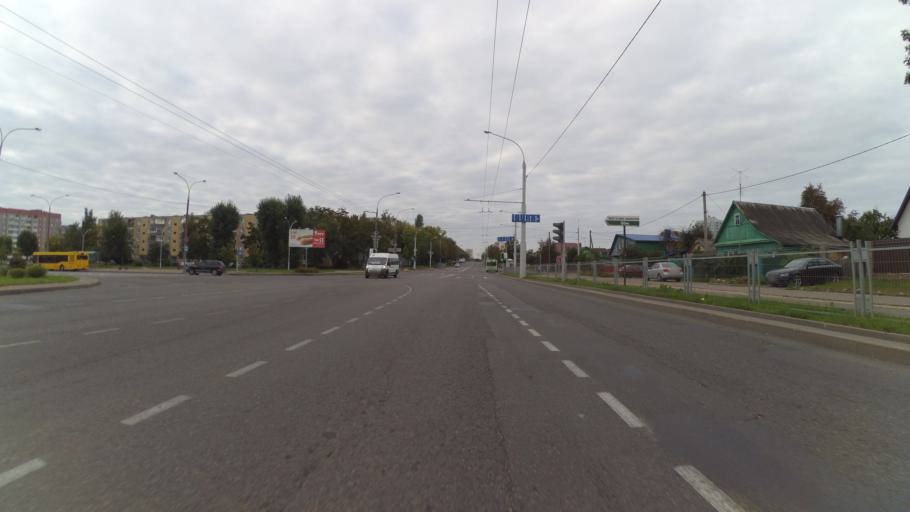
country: BY
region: Minsk
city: Vyaliki Trastsyanets
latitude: 53.8708
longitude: 27.6836
